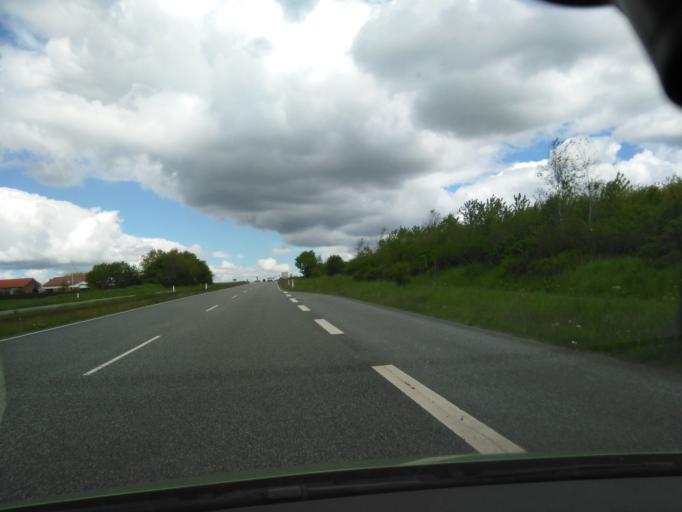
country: DK
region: Central Jutland
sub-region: Arhus Kommune
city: Solbjerg
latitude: 56.0502
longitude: 10.0831
